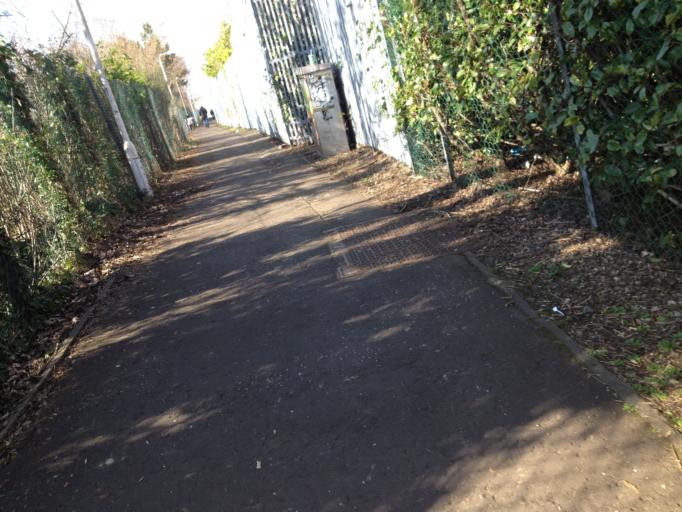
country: GB
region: Scotland
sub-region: South Lanarkshire
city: Hamilton
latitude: 55.7792
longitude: -4.0547
